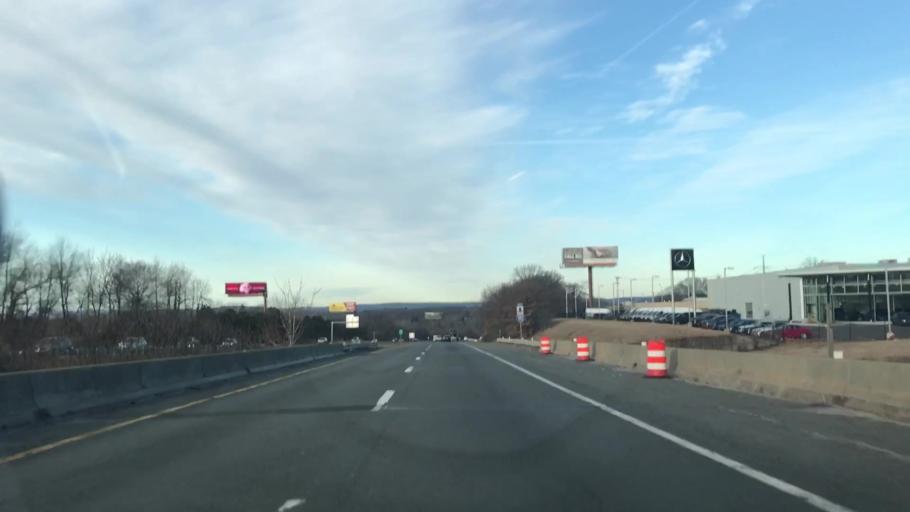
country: US
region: Massachusetts
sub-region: Hampden County
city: North Chicopee
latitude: 42.1623
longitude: -72.5470
